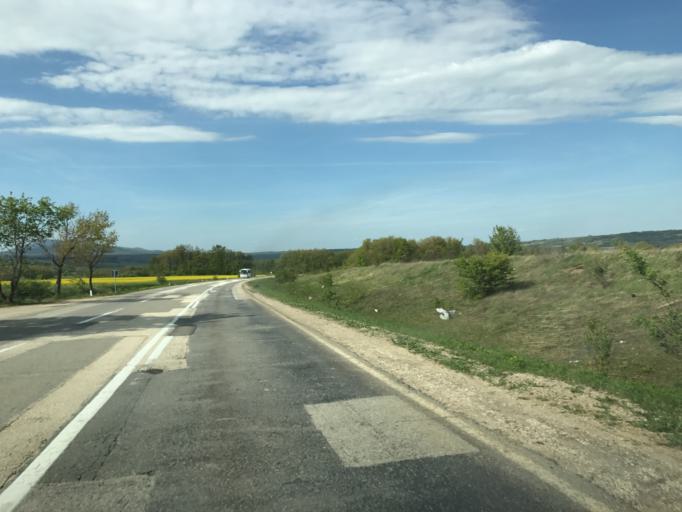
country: RS
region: Central Serbia
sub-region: Zajecarski Okrug
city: Zajecar
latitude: 44.0708
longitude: 22.3339
